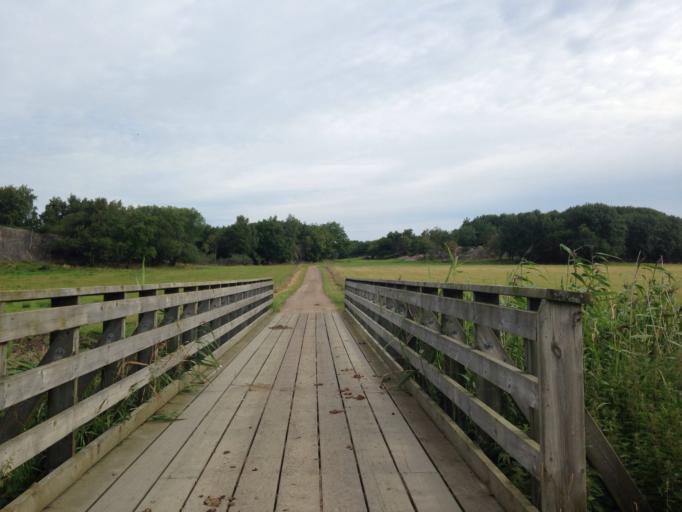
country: SE
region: Vaestra Goetaland
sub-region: Kungalvs Kommun
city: Kungalv
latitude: 57.8085
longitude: 11.8854
